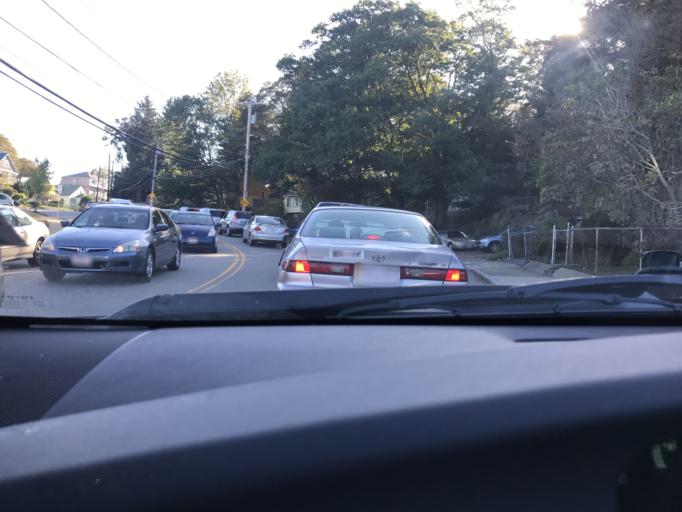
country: US
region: Massachusetts
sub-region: Suffolk County
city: Jamaica Plain
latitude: 42.2776
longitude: -71.1247
